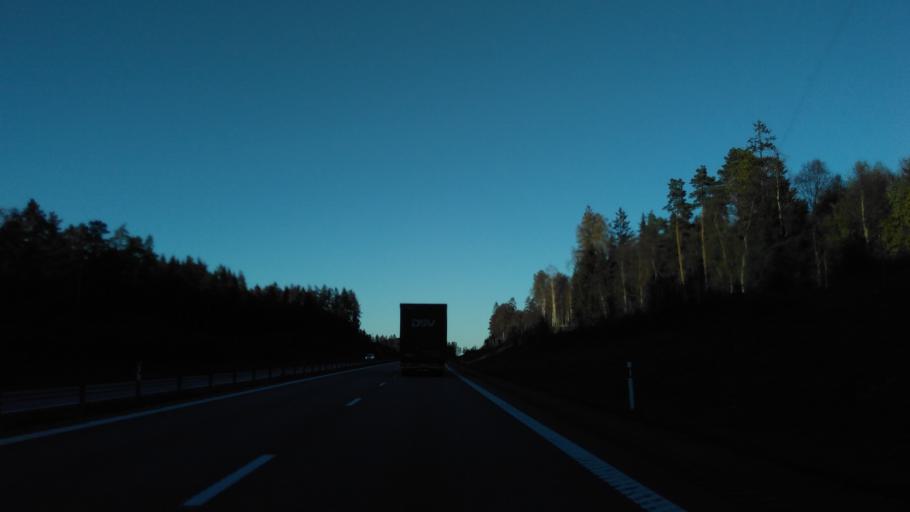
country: SE
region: Vaestra Goetaland
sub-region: Boras Kommun
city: Dalsjofors
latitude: 57.7715
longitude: 13.1141
